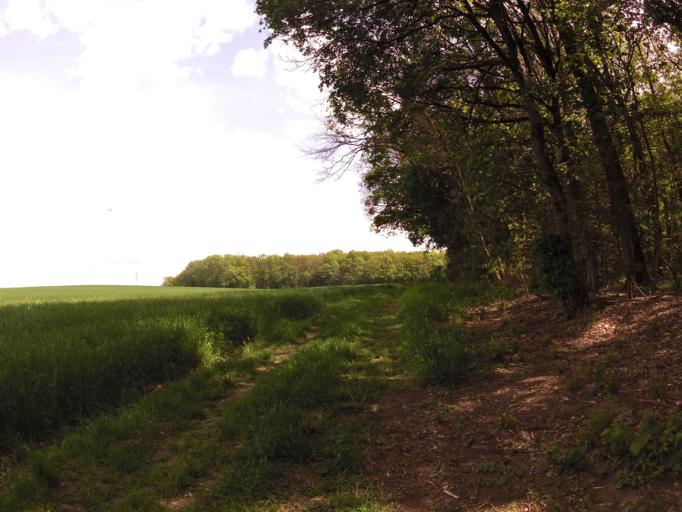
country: DE
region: Bavaria
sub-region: Regierungsbezirk Unterfranken
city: Theilheim
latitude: 49.7471
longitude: 10.0370
